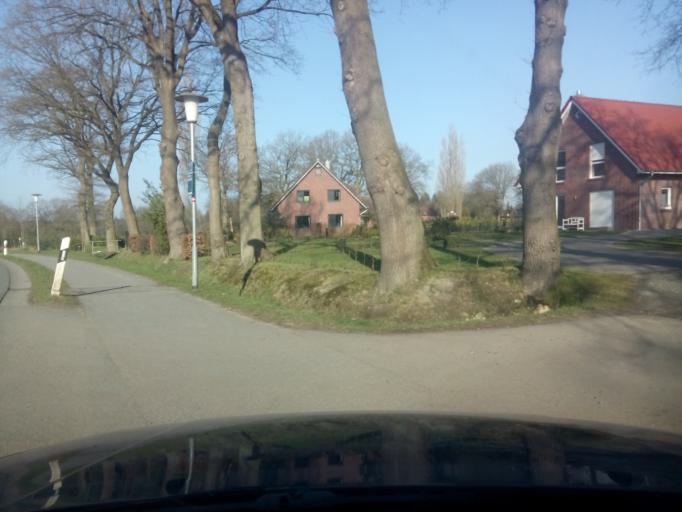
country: DE
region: Lower Saxony
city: Osterholz-Scharmbeck
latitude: 53.2240
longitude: 8.7557
